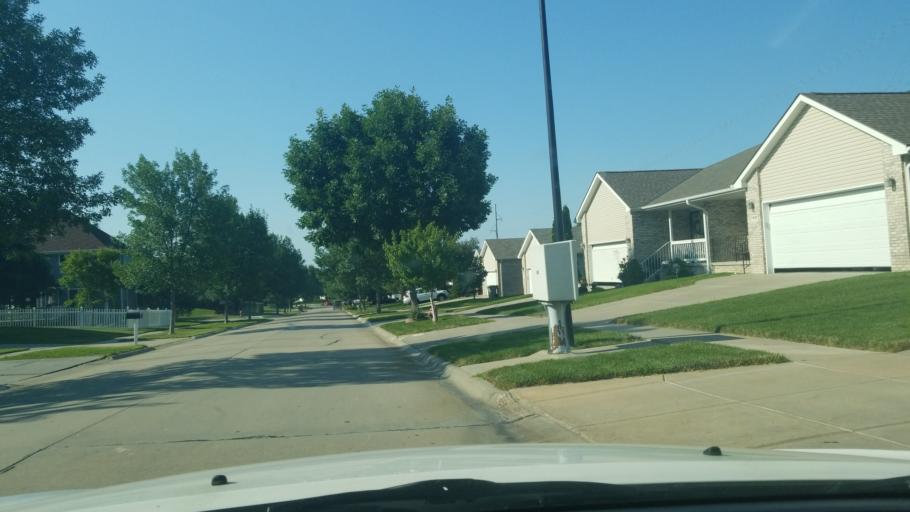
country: US
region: Nebraska
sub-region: Lancaster County
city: Lincoln
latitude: 40.7509
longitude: -96.6109
